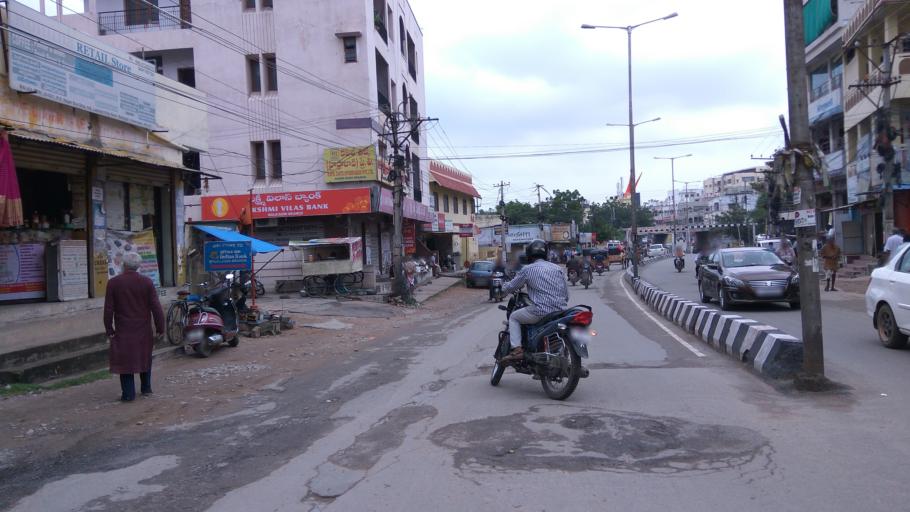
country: IN
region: Telangana
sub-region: Hyderabad
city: Malkajgiri
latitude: 17.4558
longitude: 78.5359
